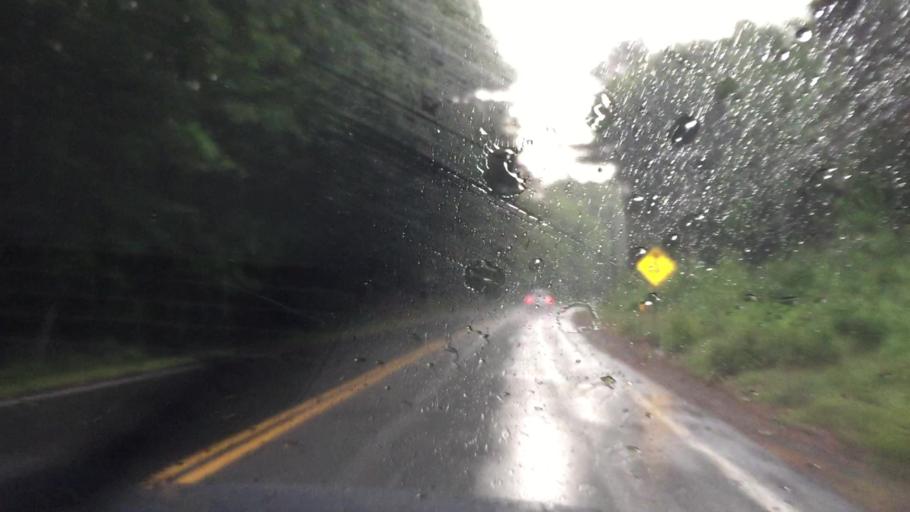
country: US
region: New Hampshire
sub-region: Grafton County
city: Holderness
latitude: 43.7207
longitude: -71.5431
